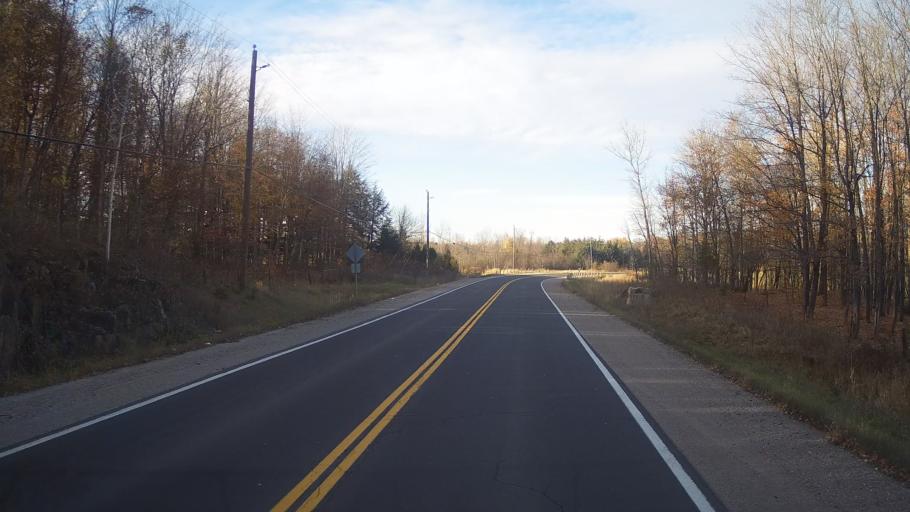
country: CA
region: Ontario
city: Perth
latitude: 44.8210
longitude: -76.3179
